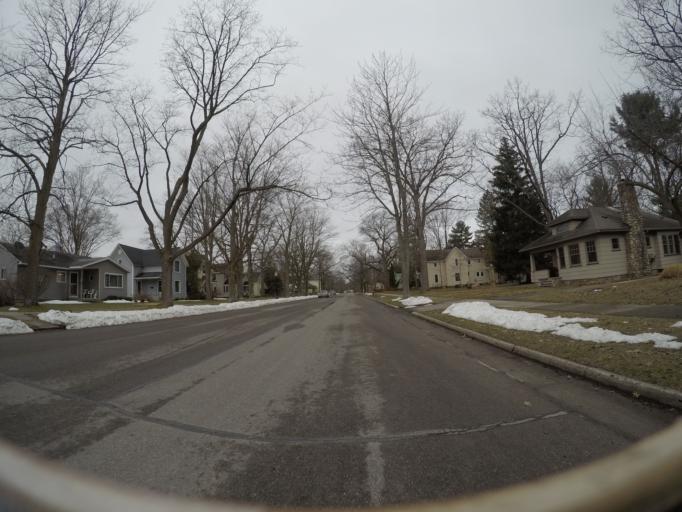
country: US
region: Michigan
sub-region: Grand Traverse County
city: Traverse City
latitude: 44.7606
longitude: -85.6027
